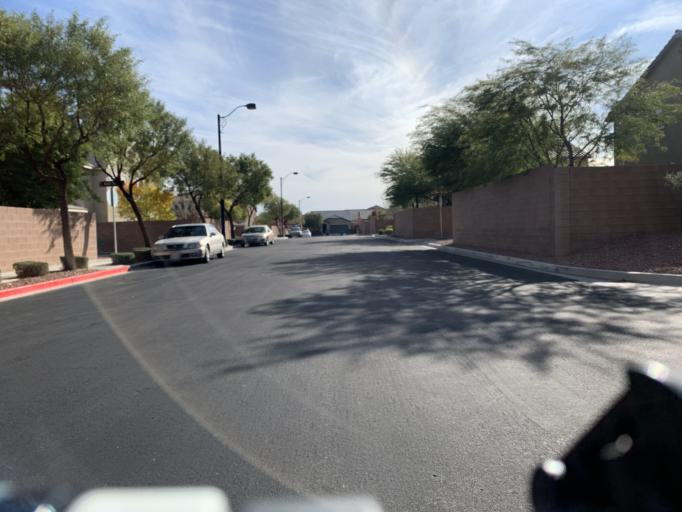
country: US
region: Nevada
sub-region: Clark County
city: Summerlin South
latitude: 36.2969
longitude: -115.3319
